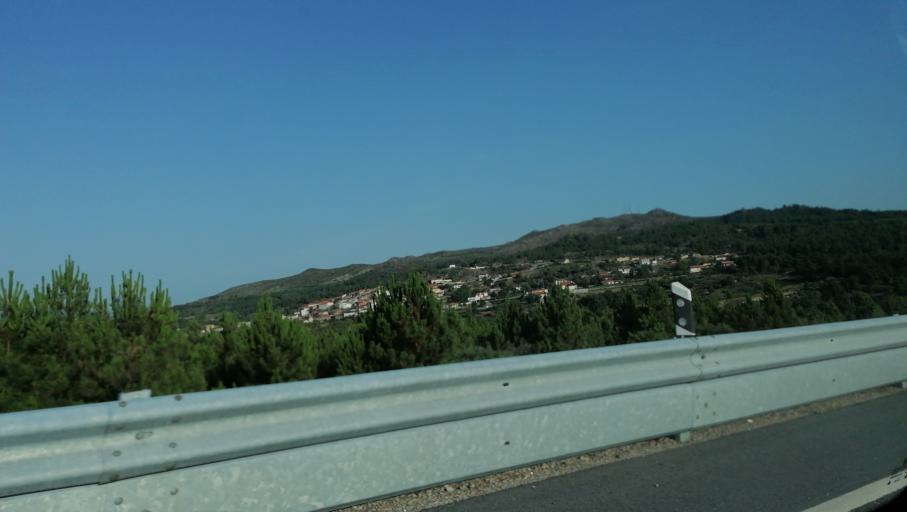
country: PT
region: Vila Real
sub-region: Murca
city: Murca
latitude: 41.3577
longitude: -7.4927
